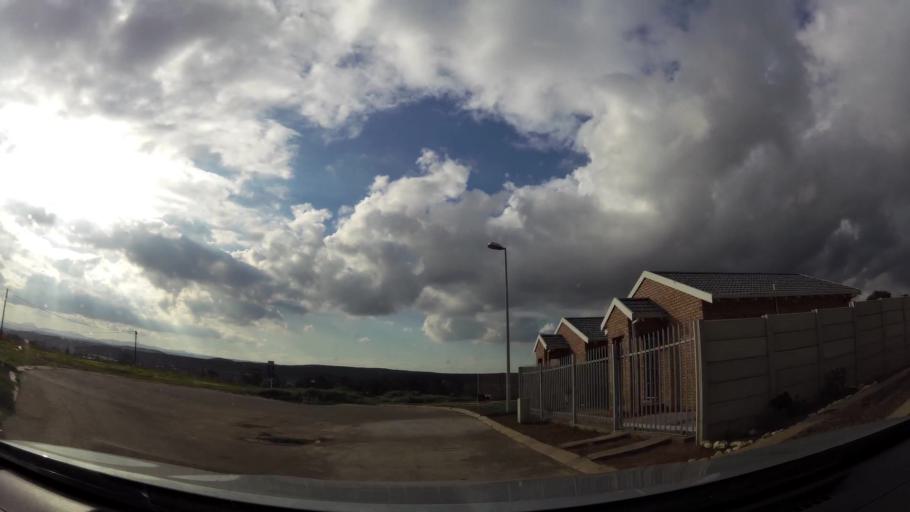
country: ZA
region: Eastern Cape
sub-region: Nelson Mandela Bay Metropolitan Municipality
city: Uitenhage
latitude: -33.7983
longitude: 25.4555
